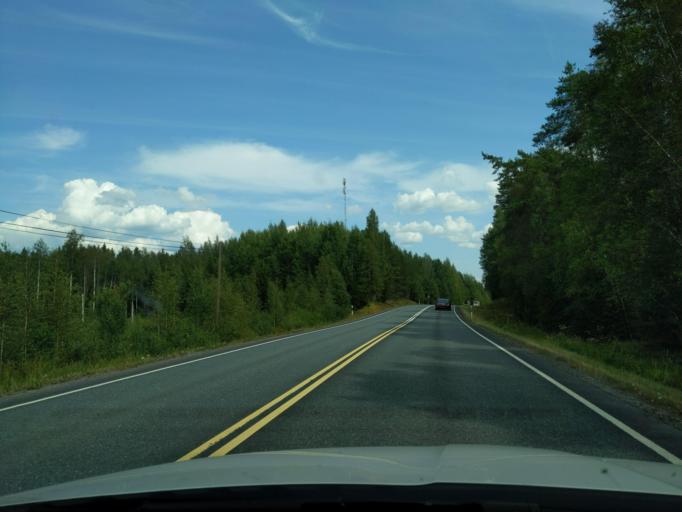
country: FI
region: Haeme
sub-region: Haemeenlinna
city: Tuulos
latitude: 61.0970
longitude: 24.8184
